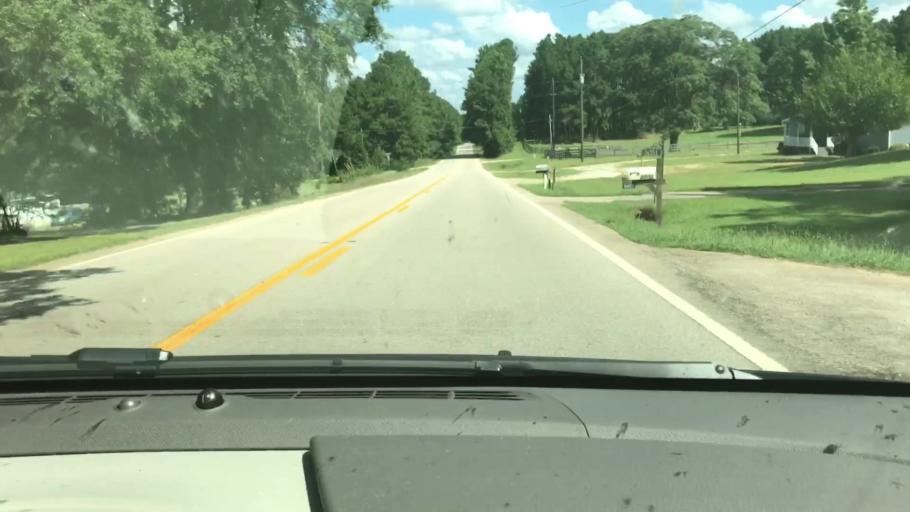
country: US
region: Georgia
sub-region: Troup County
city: La Grange
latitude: 32.9187
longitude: -85.0199
